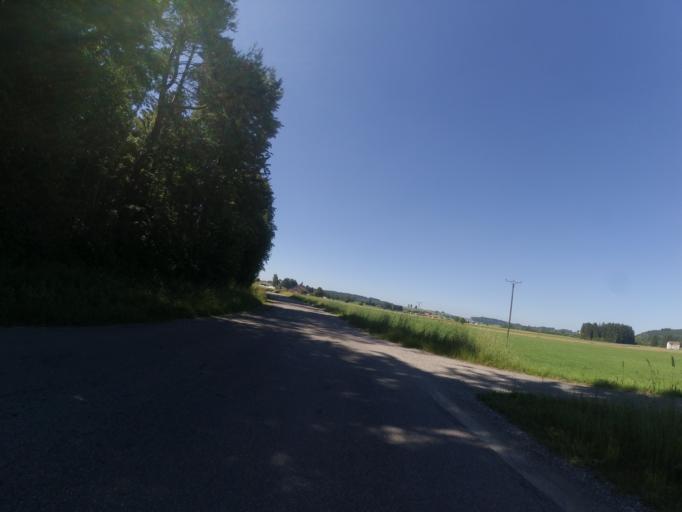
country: DE
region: Baden-Wuerttemberg
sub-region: Tuebingen Region
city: Leutkirch im Allgau
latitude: 47.8511
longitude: 9.9915
